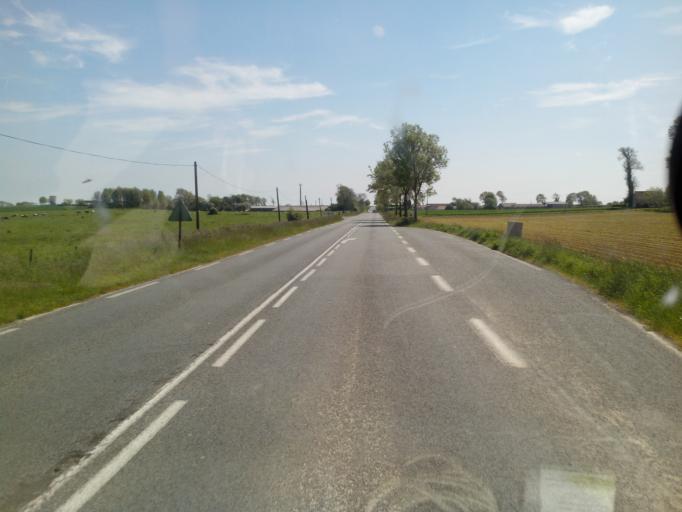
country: FR
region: Nord-Pas-de-Calais
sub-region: Departement du Pas-de-Calais
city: Samer
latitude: 50.6054
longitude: 1.7440
